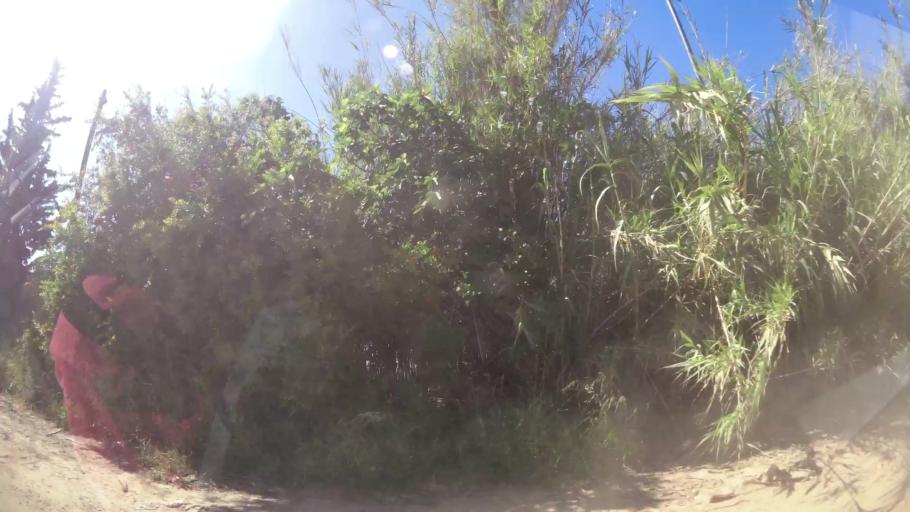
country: MA
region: Oriental
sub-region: Berkane-Taourirt
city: Berkane
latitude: 34.9469
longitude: -2.3277
